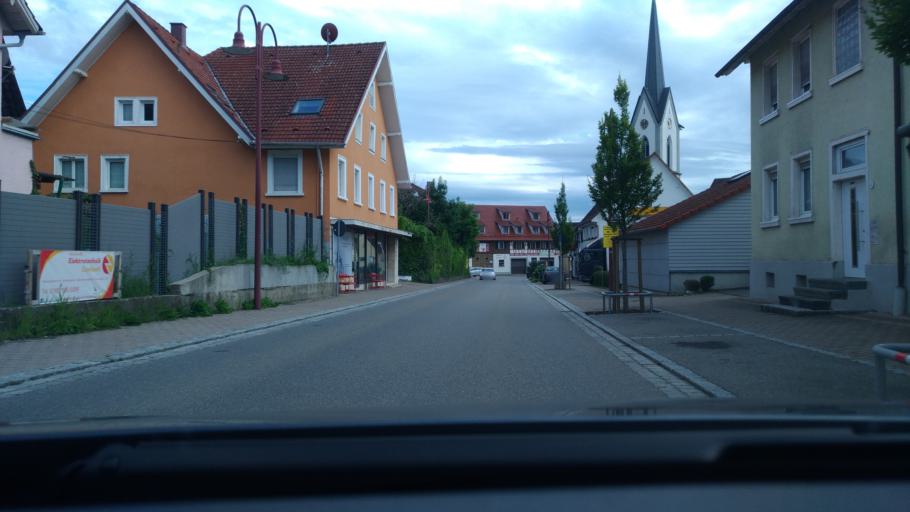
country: DE
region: Baden-Wuerttemberg
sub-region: Freiburg Region
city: Bodman-Ludwigshafen
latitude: 47.8203
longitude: 9.0592
